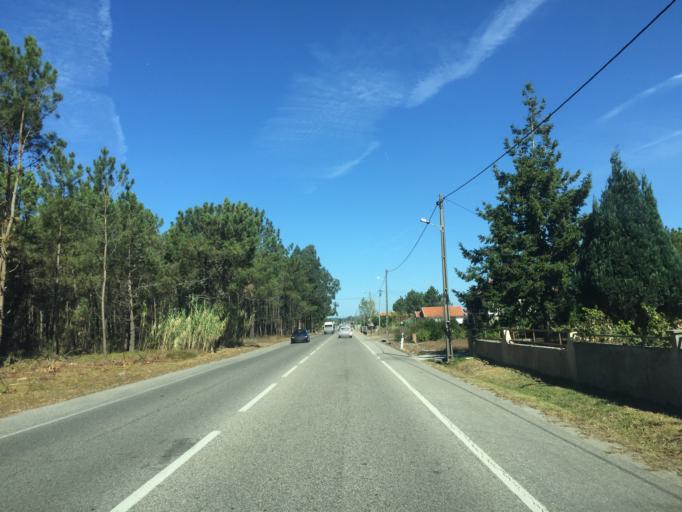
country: PT
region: Coimbra
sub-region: Figueira da Foz
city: Alhadas
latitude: 40.2234
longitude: -8.8056
